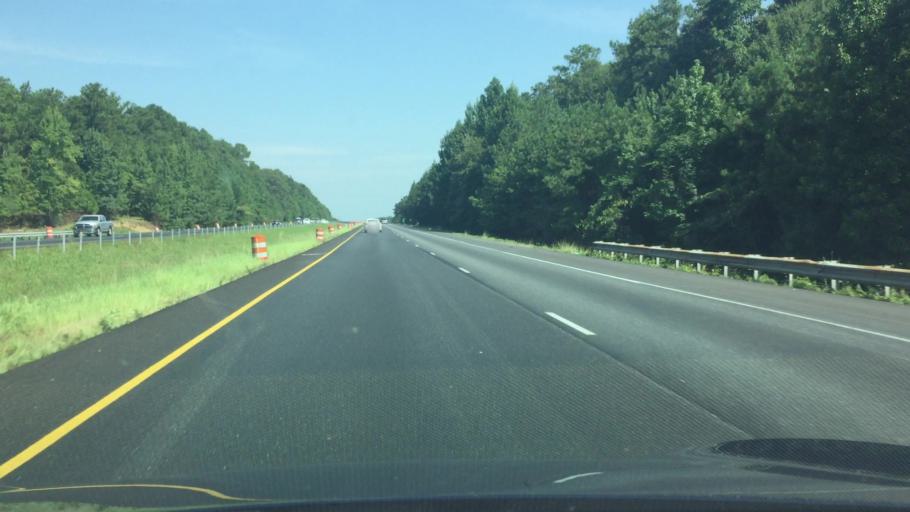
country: US
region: Alabama
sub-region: Autauga County
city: Marbury
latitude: 32.7148
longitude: -86.5290
